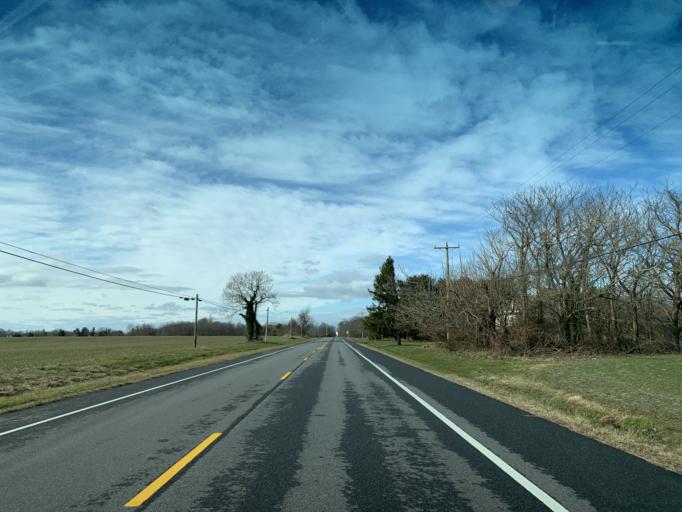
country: US
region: Maryland
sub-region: Kent County
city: Chestertown
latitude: 39.3262
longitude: -76.0341
